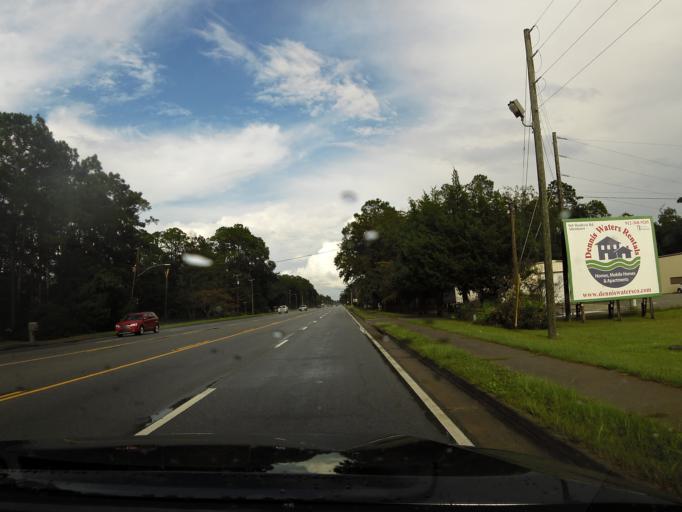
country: US
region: Georgia
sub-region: Liberty County
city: Walthourville
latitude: 31.7774
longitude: -81.6259
